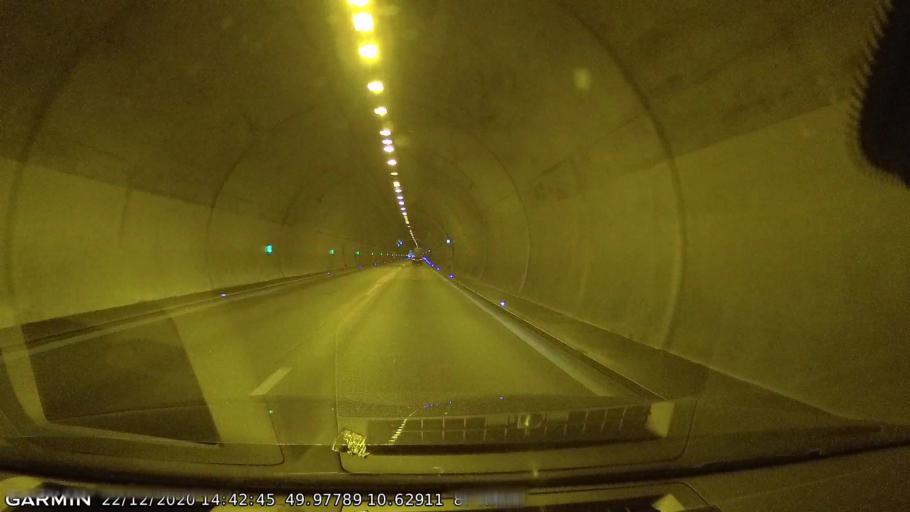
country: DE
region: Bavaria
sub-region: Regierungsbezirk Unterfranken
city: Eltmann
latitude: 49.9779
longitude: 10.6293
